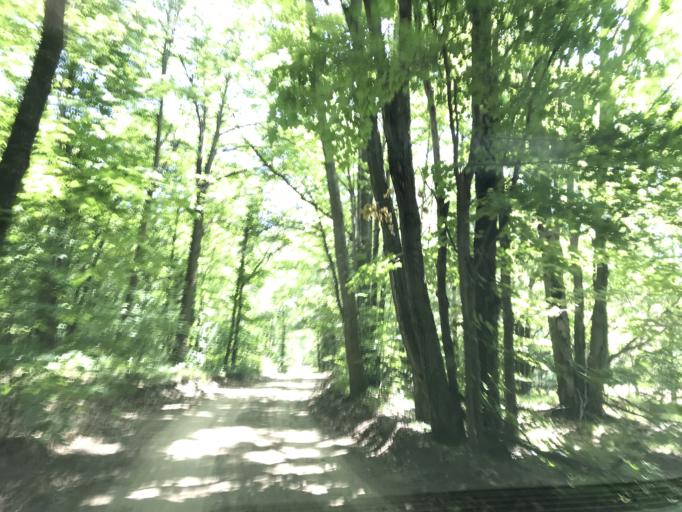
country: US
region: Michigan
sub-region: Missaukee County
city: Lake City
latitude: 44.2790
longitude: -85.0387
